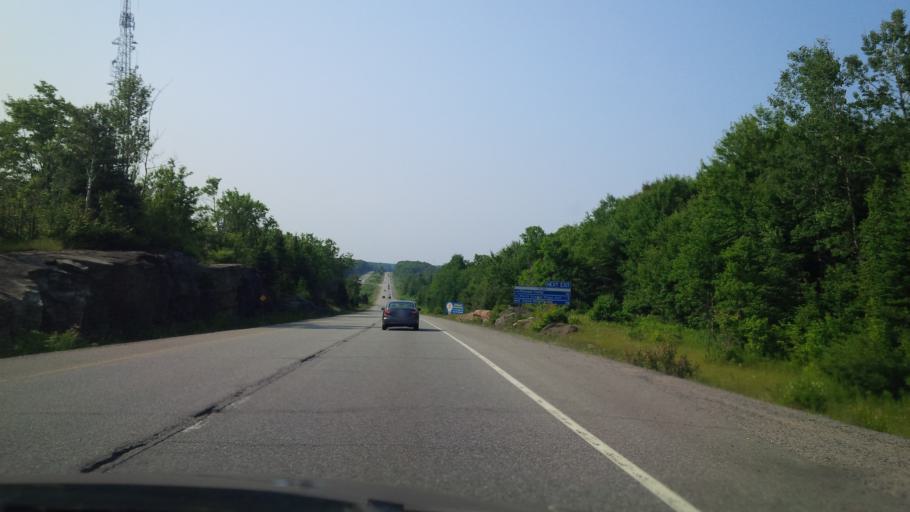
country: CA
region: Ontario
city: Huntsville
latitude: 45.2050
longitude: -79.3150
